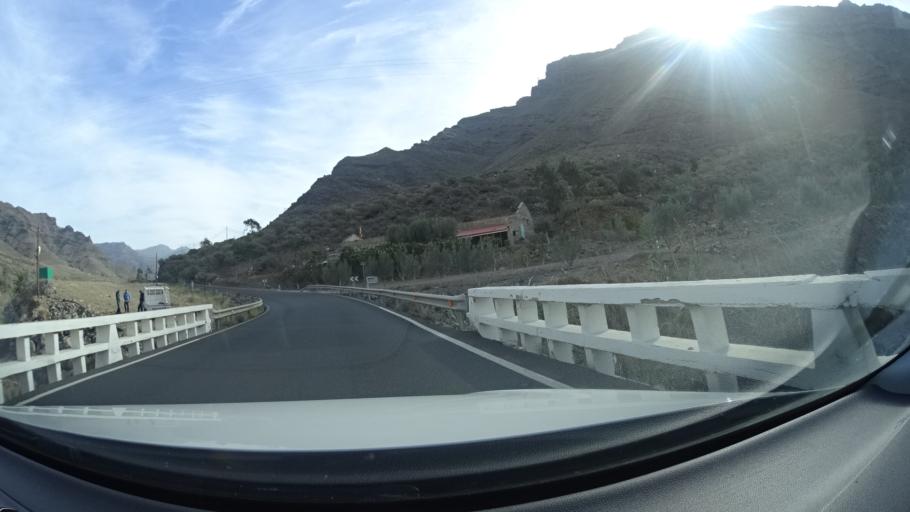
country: ES
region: Canary Islands
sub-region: Provincia de Las Palmas
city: Mogan
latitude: 27.8654
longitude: -15.7407
